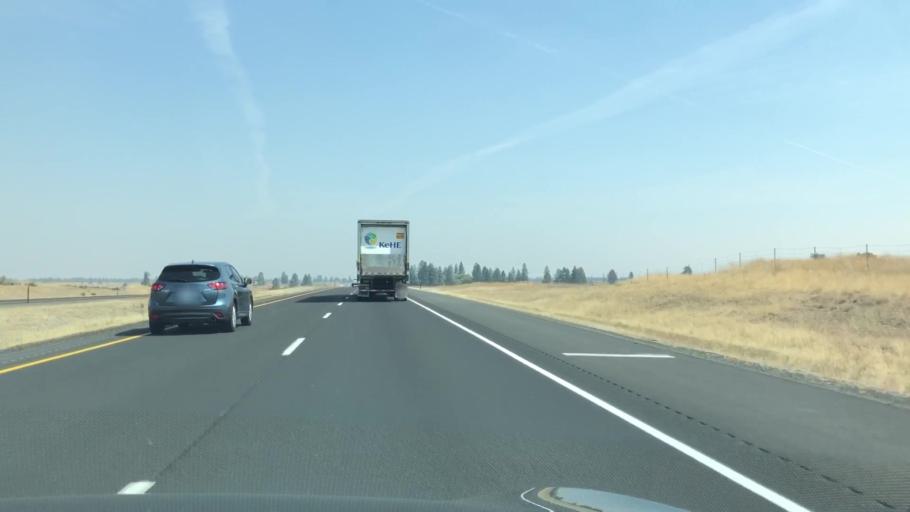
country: US
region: Washington
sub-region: Spokane County
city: Medical Lake
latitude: 47.3859
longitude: -117.8545
